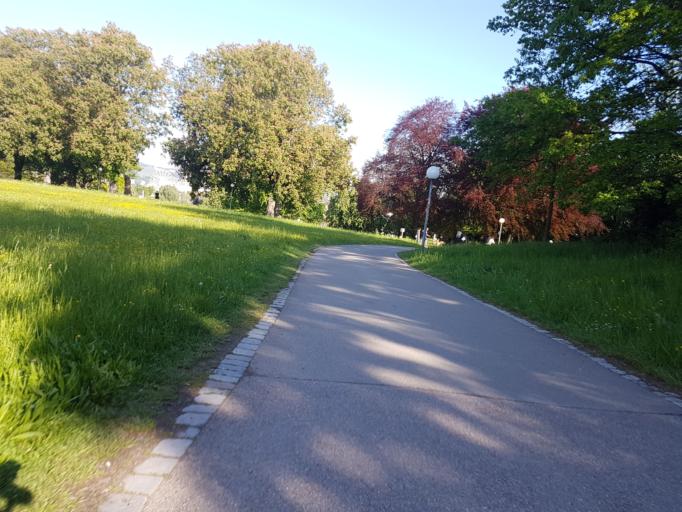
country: DE
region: Baden-Wuerttemberg
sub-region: Regierungsbezirk Stuttgart
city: Stuttgart-Ost
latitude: 48.7992
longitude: 9.2032
